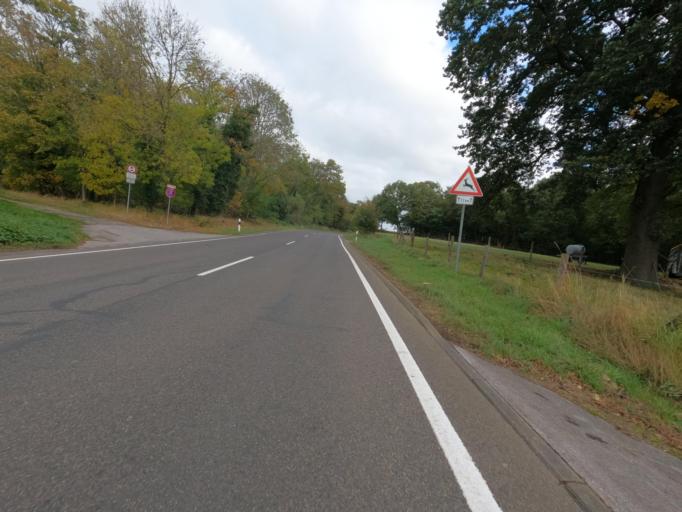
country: DE
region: North Rhine-Westphalia
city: Huckelhoven
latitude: 51.0511
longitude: 6.2536
